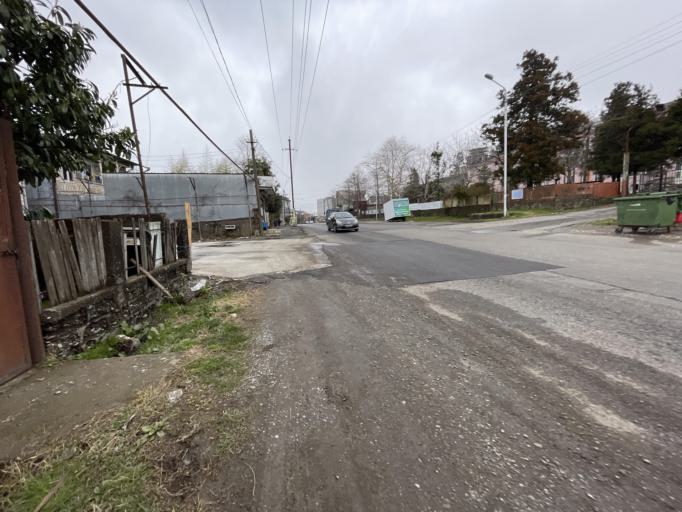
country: GE
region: Ajaria
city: Batumi
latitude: 41.6350
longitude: 41.6452
